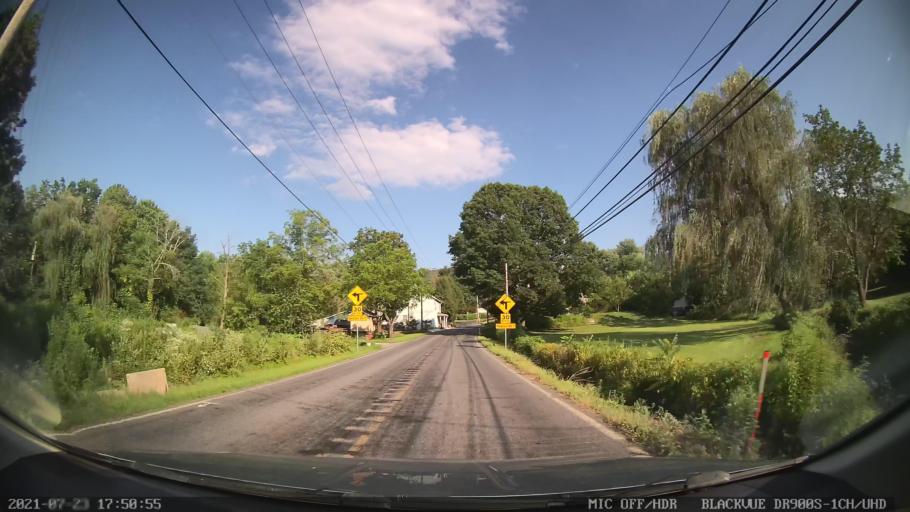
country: US
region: Pennsylvania
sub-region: Lehigh County
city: Alburtis
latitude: 40.4955
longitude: -75.5914
